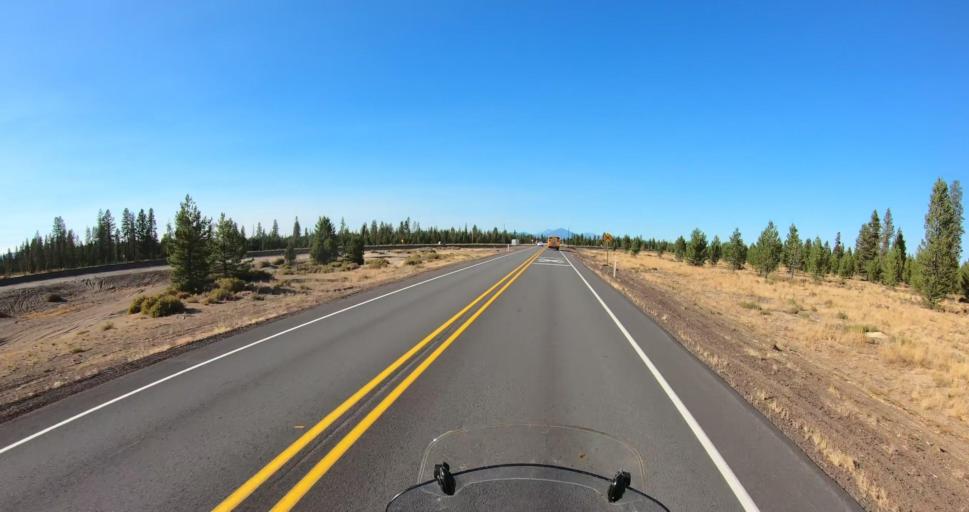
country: US
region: Oregon
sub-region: Deschutes County
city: La Pine
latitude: 43.6055
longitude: -121.5004
